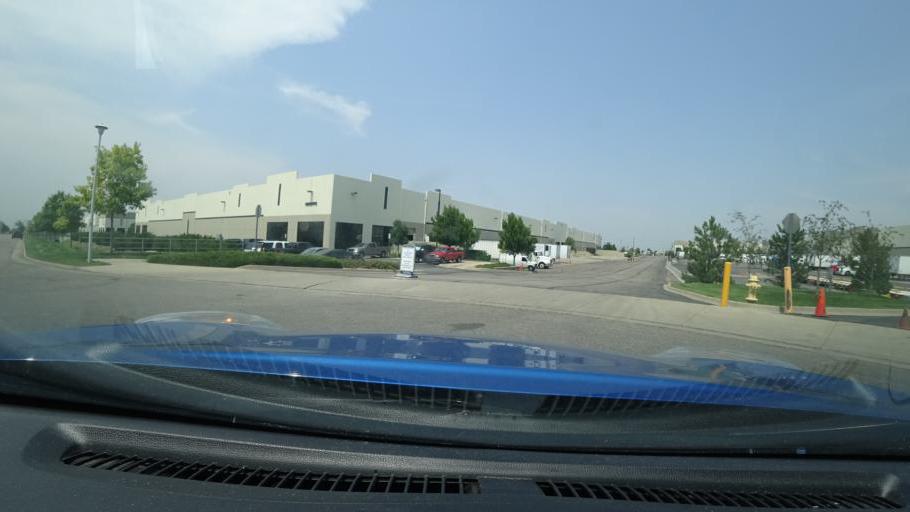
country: US
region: Colorado
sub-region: Adams County
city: Aurora
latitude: 39.7637
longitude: -104.7567
